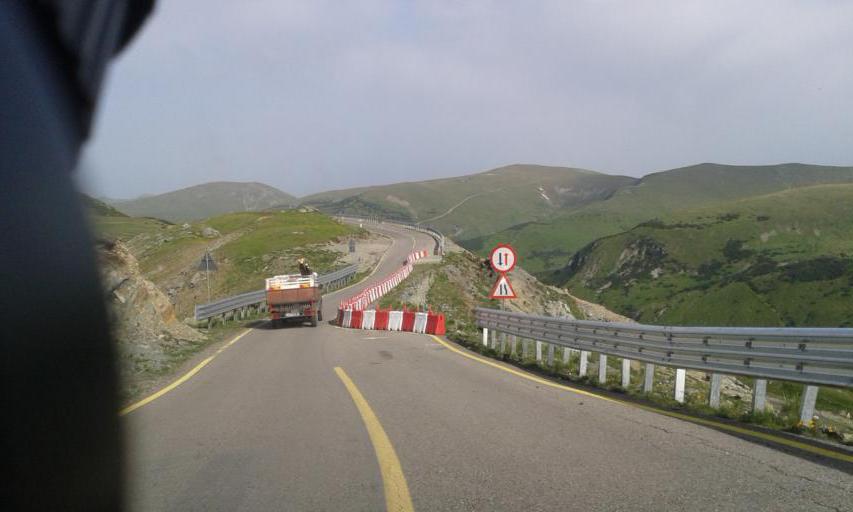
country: RO
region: Gorj
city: Novaci-Straini
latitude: 45.3599
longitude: 23.6612
